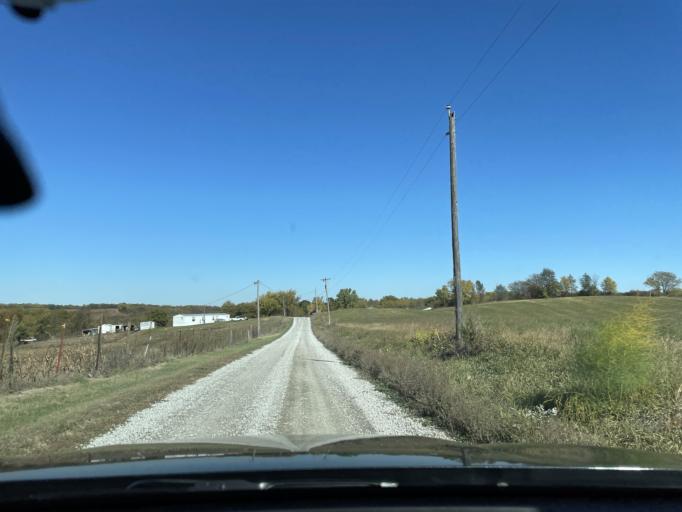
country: US
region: Missouri
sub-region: Andrew County
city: Savannah
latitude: 39.9317
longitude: -94.8805
